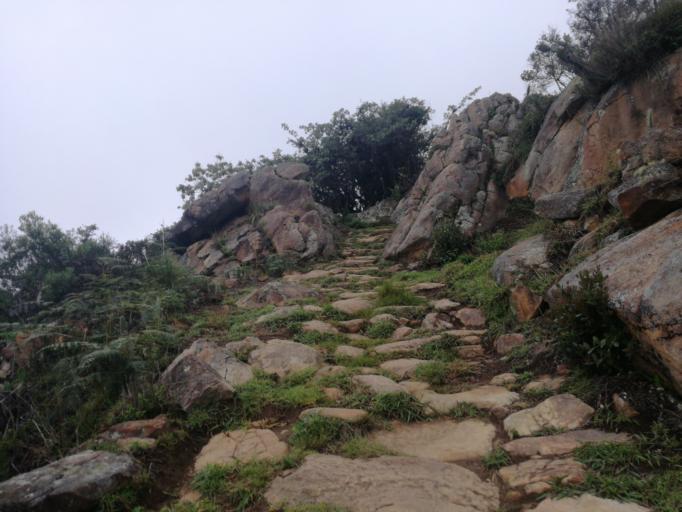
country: CO
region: Boyaca
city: Socha Viejo
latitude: 6.0021
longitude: -72.6853
